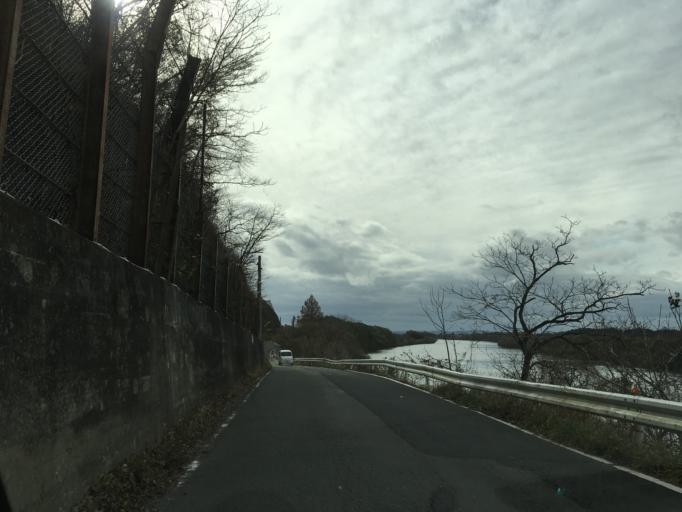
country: JP
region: Iwate
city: Ichinoseki
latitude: 38.7470
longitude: 141.2824
